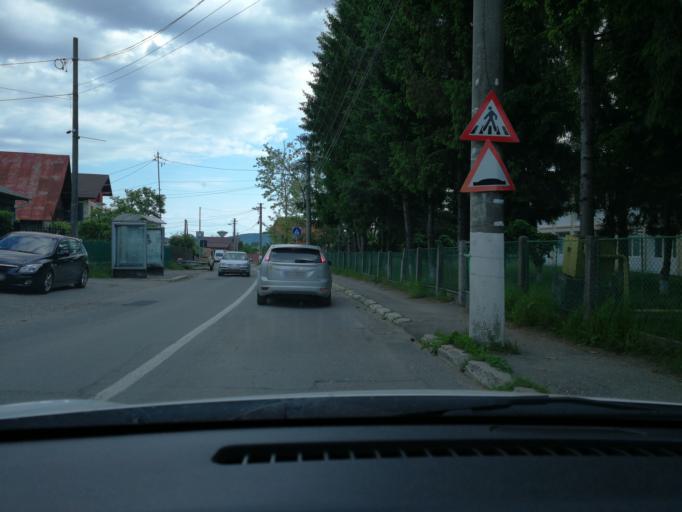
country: RO
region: Prahova
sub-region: Municipiul Campina
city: Campina
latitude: 45.1419
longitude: 25.7548
